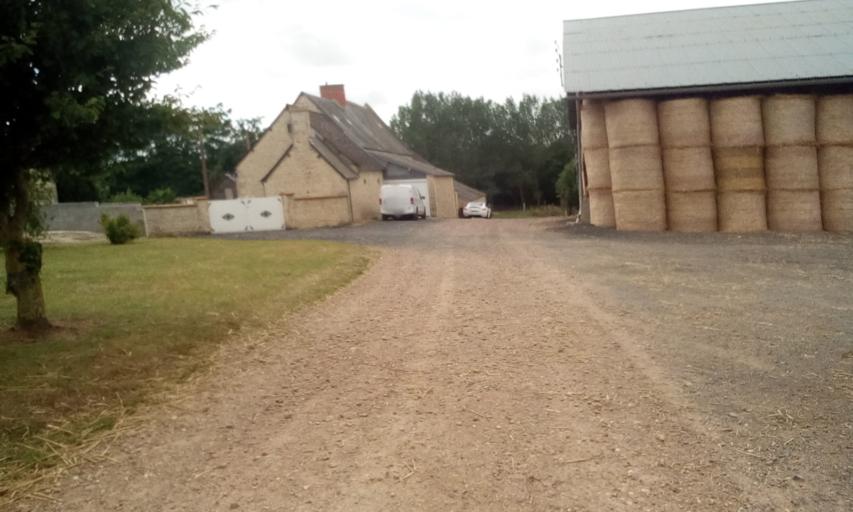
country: FR
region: Lower Normandy
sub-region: Departement du Calvados
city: Tilly-sur-Seulles
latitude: 49.2047
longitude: -0.6282
